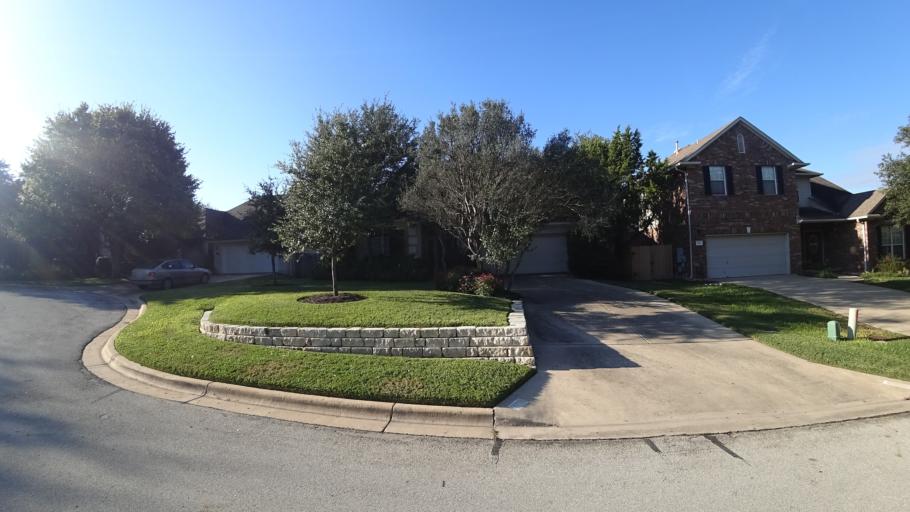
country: US
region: Texas
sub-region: Travis County
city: Hudson Bend
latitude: 30.3715
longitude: -97.8939
